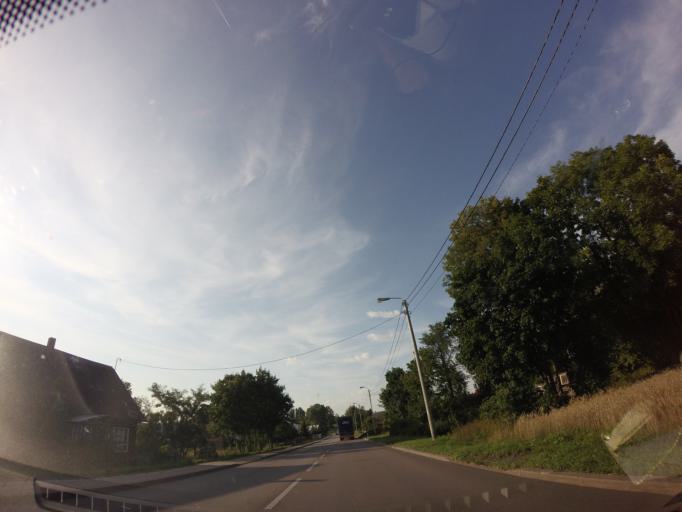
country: PL
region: Podlasie
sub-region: Powiat sokolski
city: Suchowola
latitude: 53.5377
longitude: 23.1044
